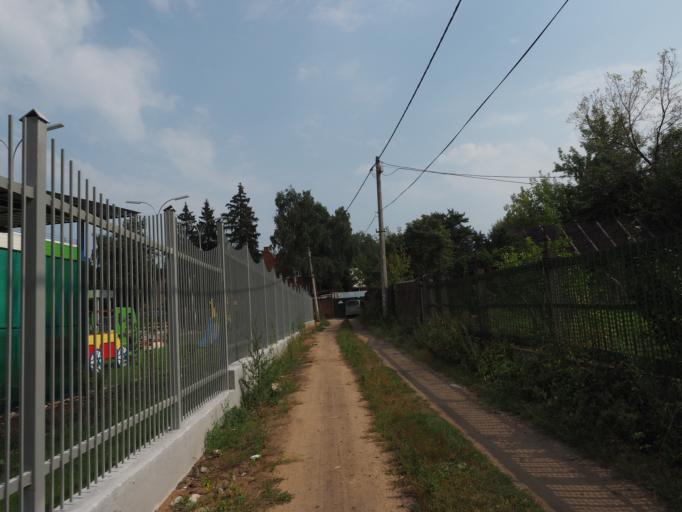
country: RU
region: Moskovskaya
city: Kraskovo
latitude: 55.6528
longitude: 37.9837
